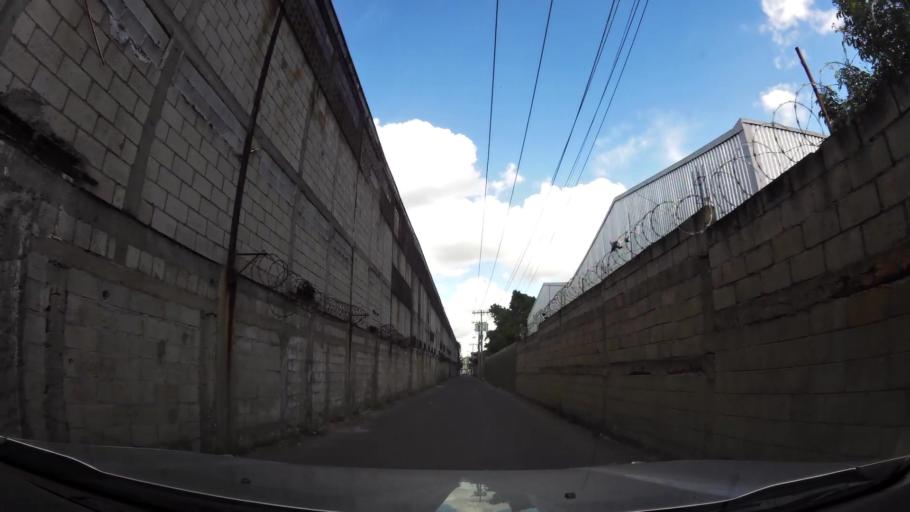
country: GT
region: Guatemala
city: Villa Nueva
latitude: 14.5296
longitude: -90.5932
